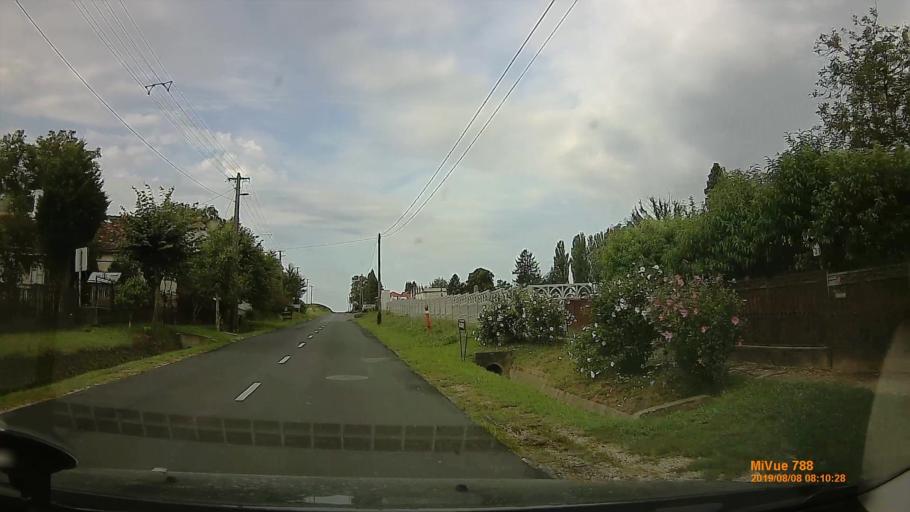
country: HU
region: Zala
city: Murakeresztur
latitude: 46.4299
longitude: 16.8894
